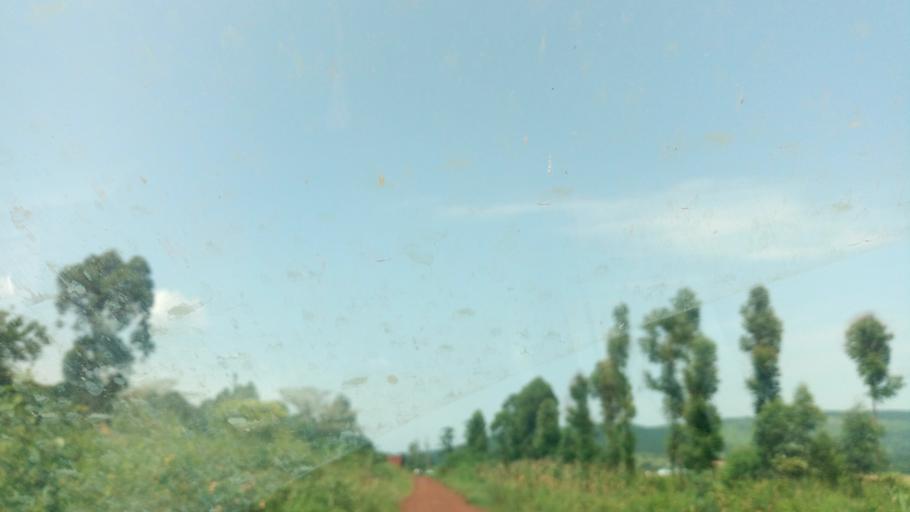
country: UG
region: Western Region
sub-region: Masindi District
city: Masindi
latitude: 1.6598
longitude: 31.8106
